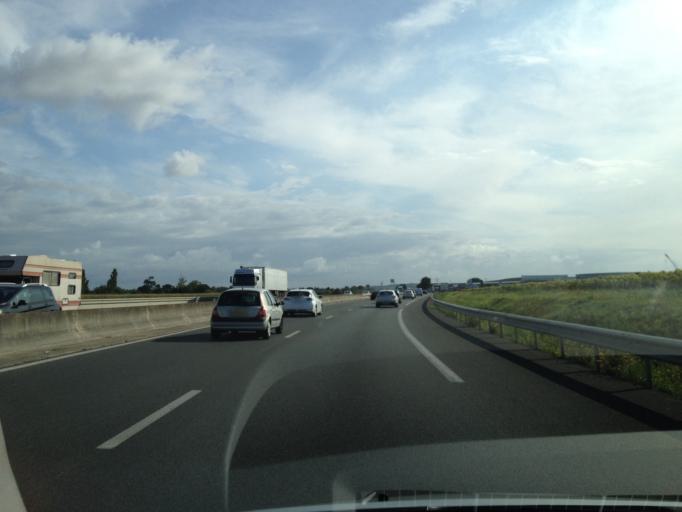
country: FR
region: Poitou-Charentes
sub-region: Departement de la Charente-Maritime
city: Aytre
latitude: 46.1257
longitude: -1.1080
